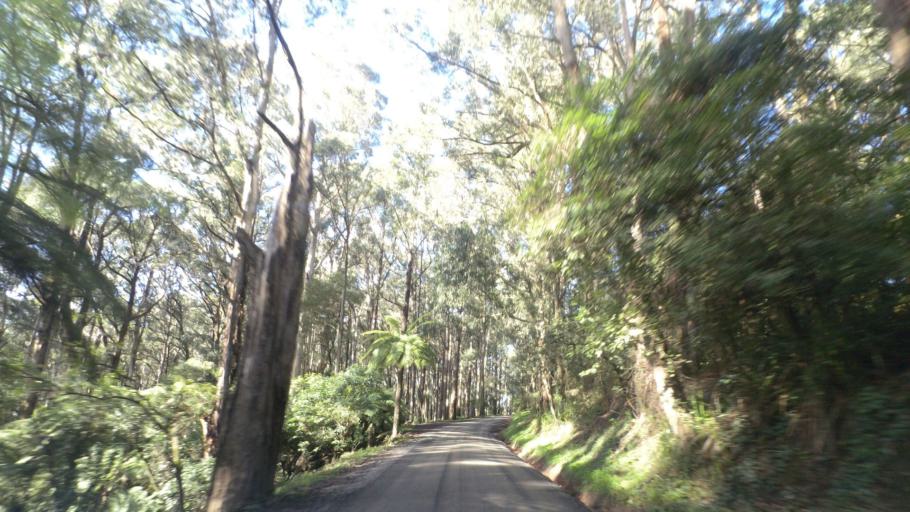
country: AU
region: Victoria
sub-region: Yarra Ranges
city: Mount Dandenong
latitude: -37.8319
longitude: 145.3696
